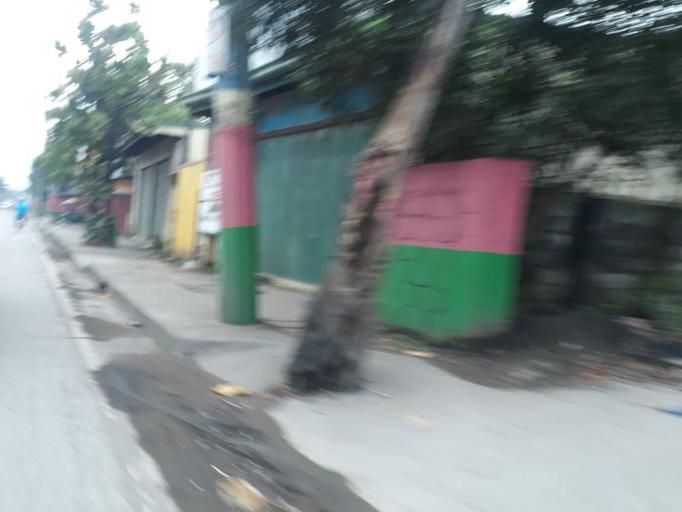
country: PH
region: Calabarzon
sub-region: Province of Rizal
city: Valenzuela
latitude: 14.6919
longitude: 120.9557
